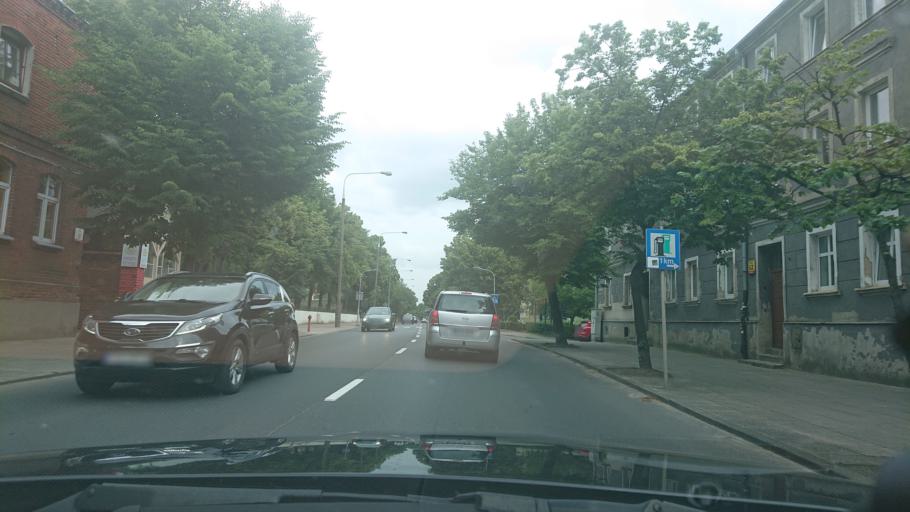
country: PL
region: Greater Poland Voivodeship
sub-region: Powiat gnieznienski
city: Gniezno
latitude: 52.5390
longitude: 17.6135
